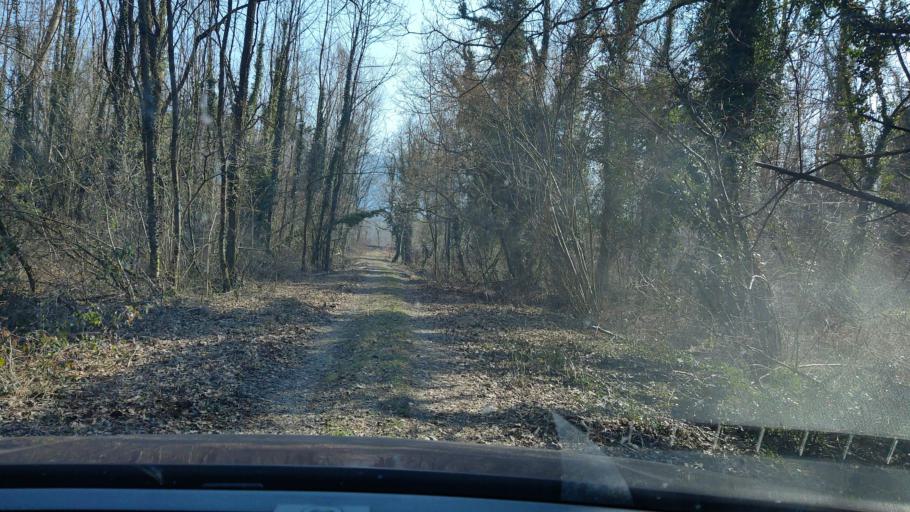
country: FR
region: Rhone-Alpes
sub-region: Departement de la Savoie
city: Cruet
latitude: 45.5110
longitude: 6.0844
